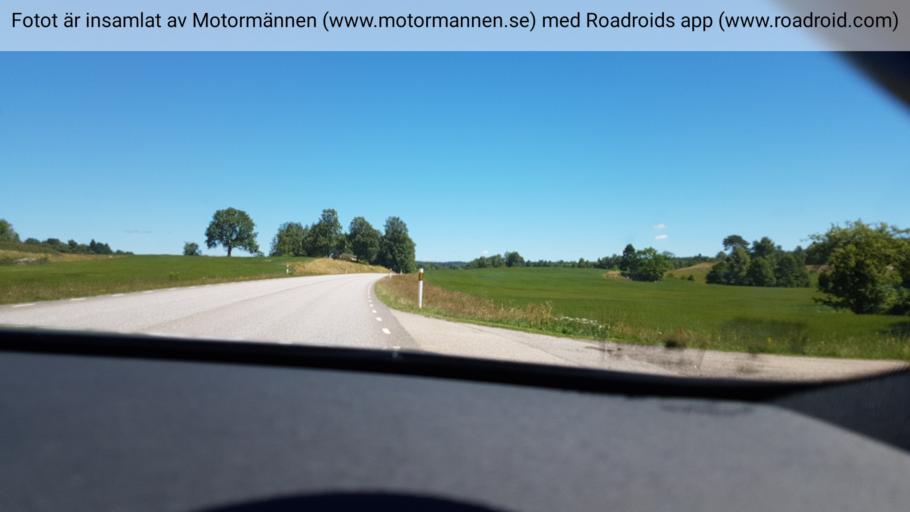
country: SE
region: Vaestra Goetaland
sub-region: Ulricehamns Kommun
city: Ulricehamn
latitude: 57.8924
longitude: 13.4429
